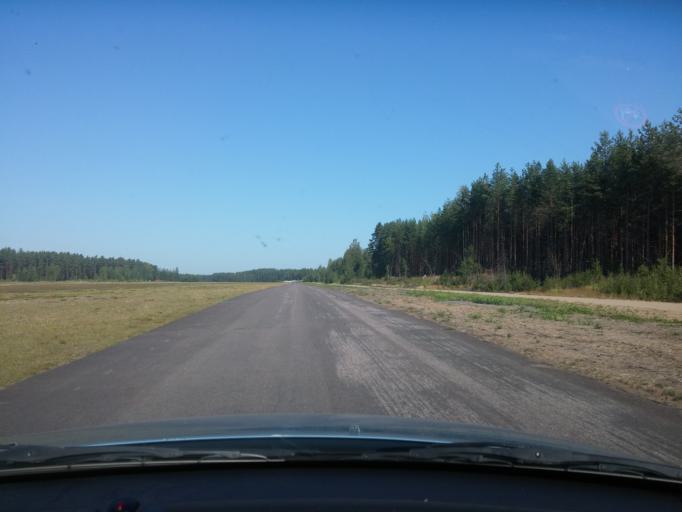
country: FI
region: Uusimaa
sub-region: Helsinki
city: Kaerkoelae
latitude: 60.7476
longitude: 24.1082
